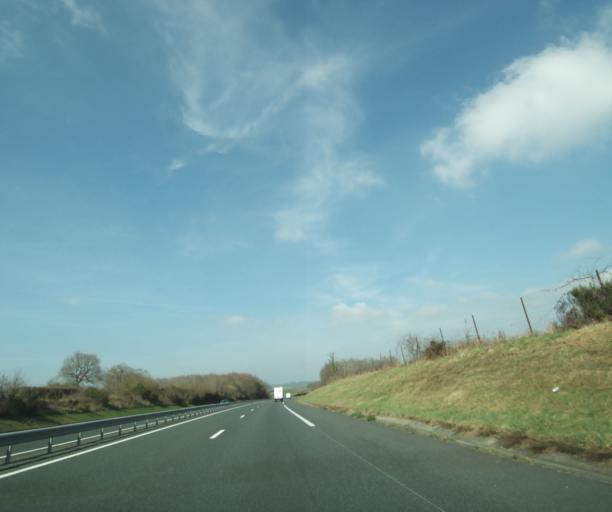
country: FR
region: Centre
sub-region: Departement de l'Indre
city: Chantome
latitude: 46.4902
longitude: 1.4985
